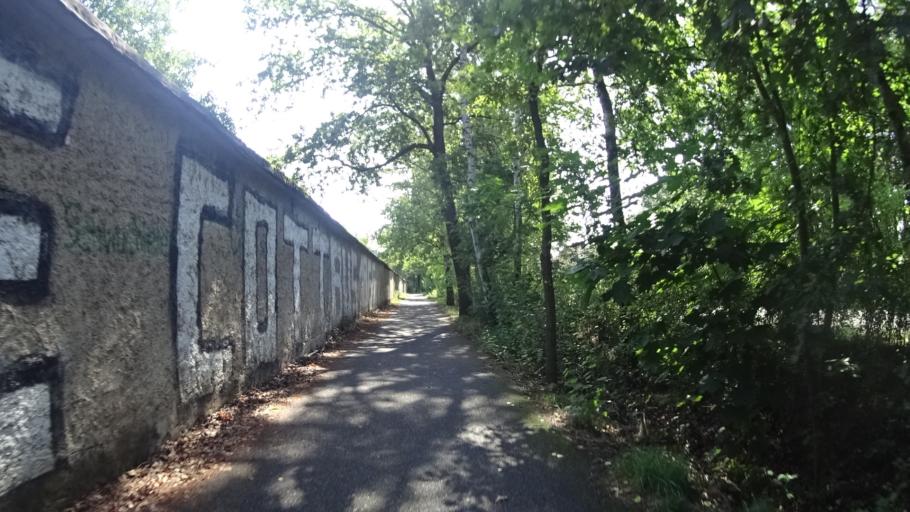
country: DE
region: Brandenburg
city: Cottbus
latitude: 51.7968
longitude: 14.2959
